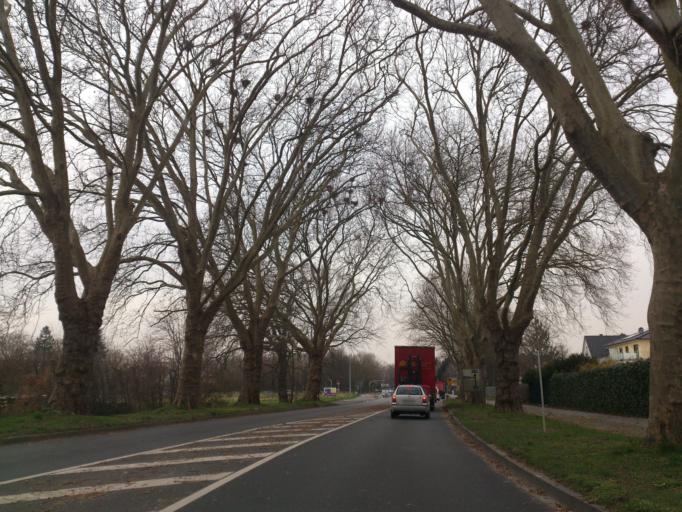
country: DE
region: North Rhine-Westphalia
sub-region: Regierungsbezirk Arnsberg
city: Soest
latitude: 51.5616
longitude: 8.1089
